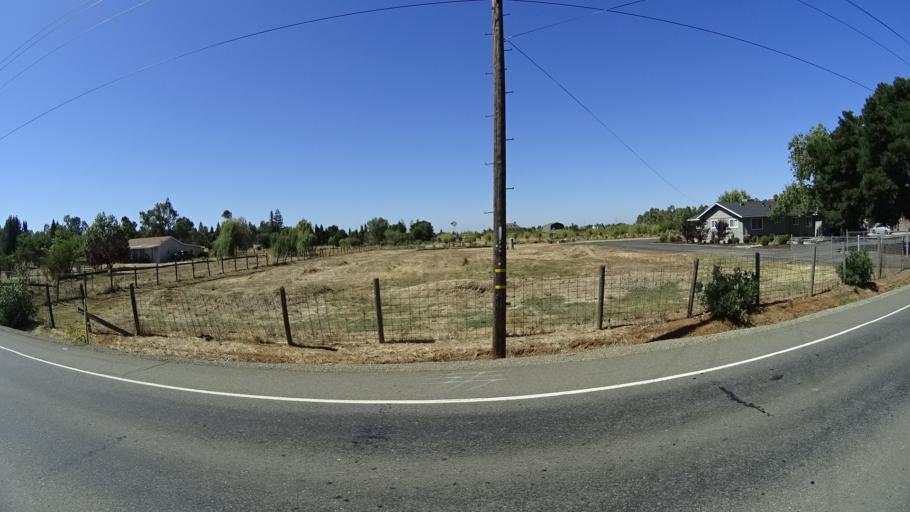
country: US
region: California
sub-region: Sacramento County
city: Vineyard
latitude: 38.4312
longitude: -121.3346
